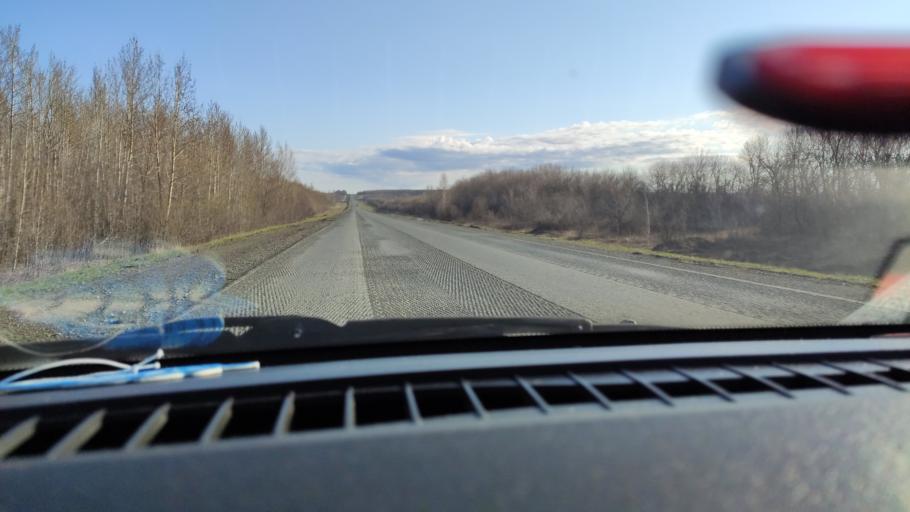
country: RU
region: Saratov
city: Dukhovnitskoye
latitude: 52.6945
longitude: 48.2476
